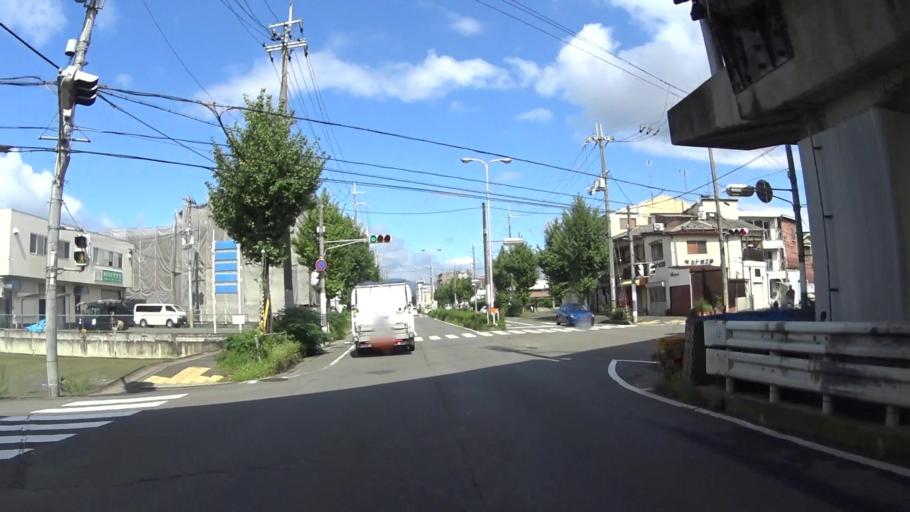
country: JP
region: Kyoto
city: Muko
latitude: 34.9694
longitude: 135.7174
